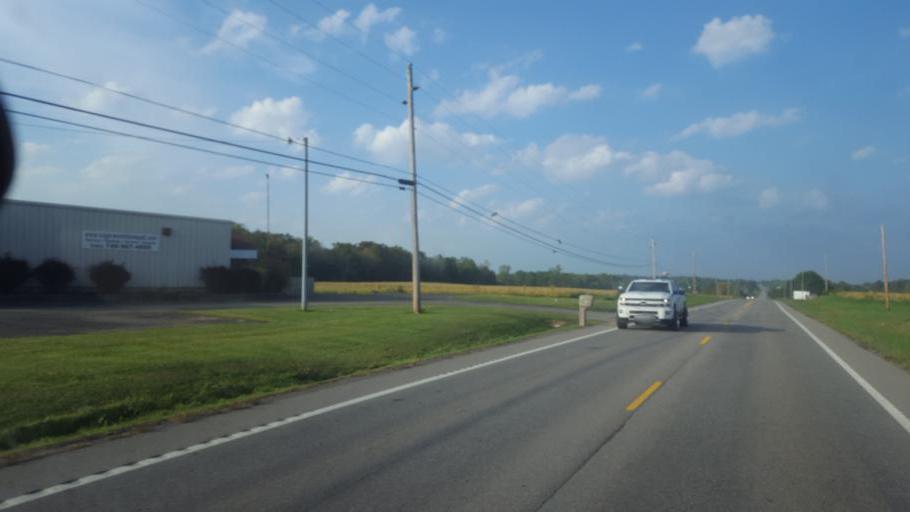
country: US
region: Ohio
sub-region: Licking County
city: Johnstown
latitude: 40.1686
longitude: -82.6542
